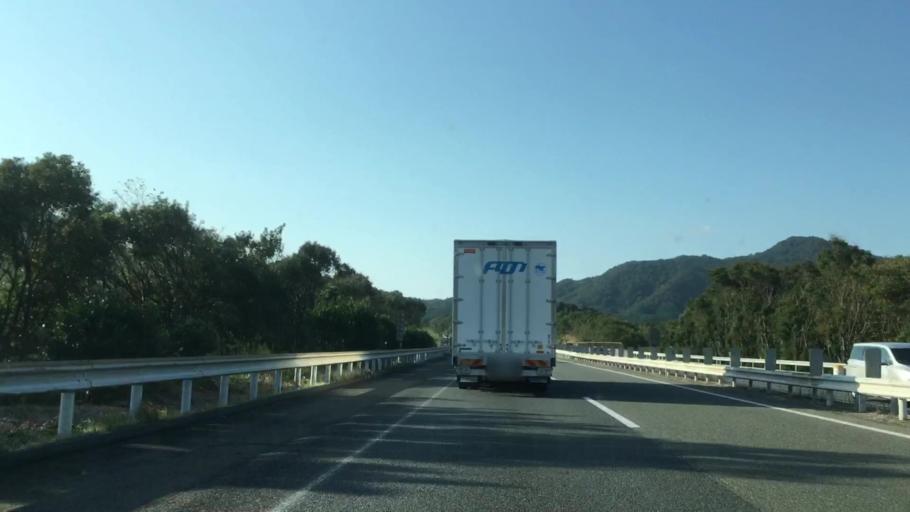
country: JP
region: Yamaguchi
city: Hofu
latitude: 34.0718
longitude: 131.4966
